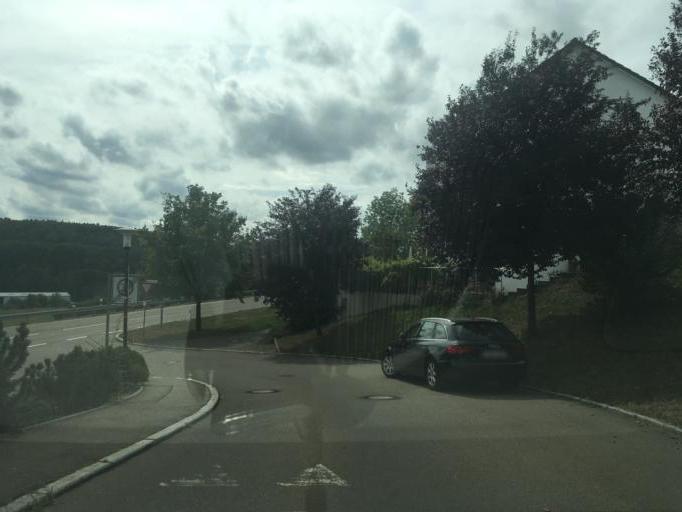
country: DE
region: Baden-Wuerttemberg
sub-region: Tuebingen Region
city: Dettenhausen
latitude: 48.6129
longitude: 9.0922
